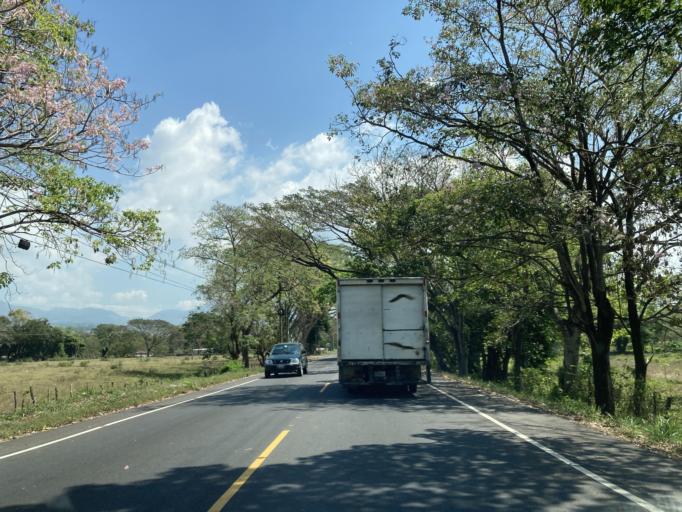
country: GT
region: Santa Rosa
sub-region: Municipio de Taxisco
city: Taxisco
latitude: 14.0942
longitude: -90.5800
